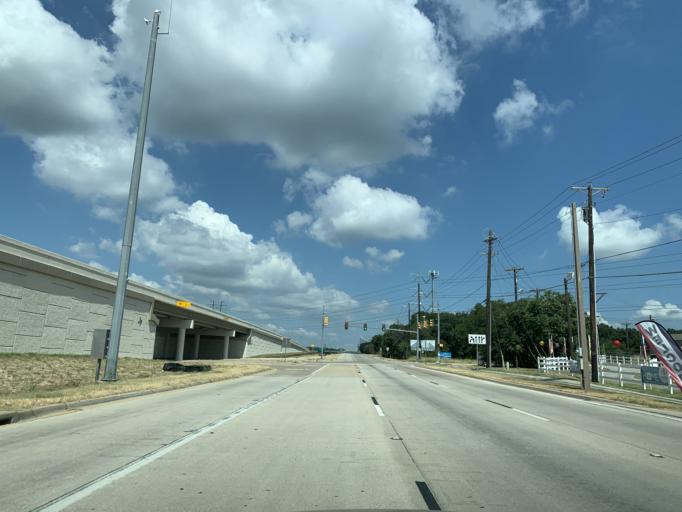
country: US
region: Texas
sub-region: Tarrant County
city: Lakeside
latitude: 32.8559
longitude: -97.5122
